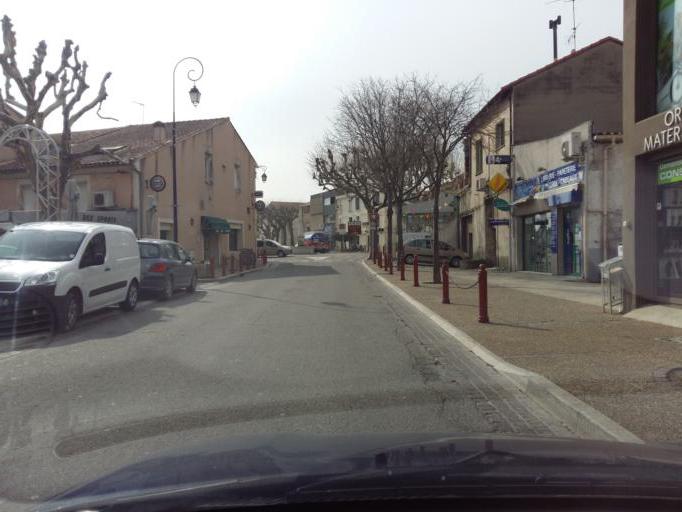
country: FR
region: Provence-Alpes-Cote d'Azur
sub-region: Departement des Bouches-du-Rhone
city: Noves
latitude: 43.8766
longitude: 4.9025
